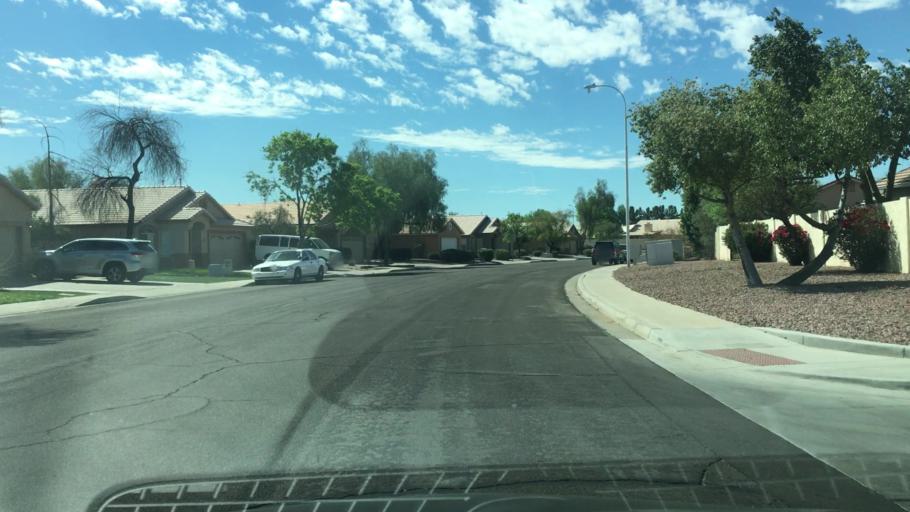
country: US
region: Arizona
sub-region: Maricopa County
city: Chandler
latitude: 33.3116
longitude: -111.8114
